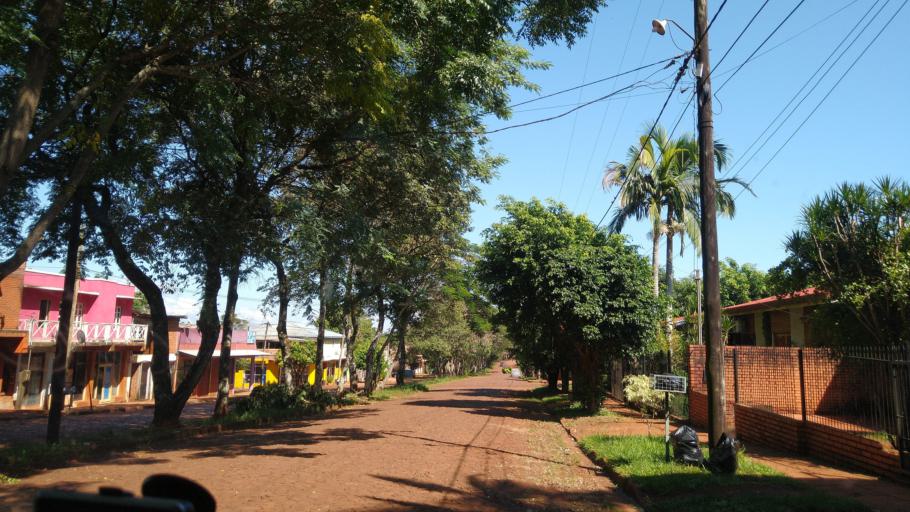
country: AR
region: Misiones
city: Puerto Libertad
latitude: -25.9686
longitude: -54.5615
